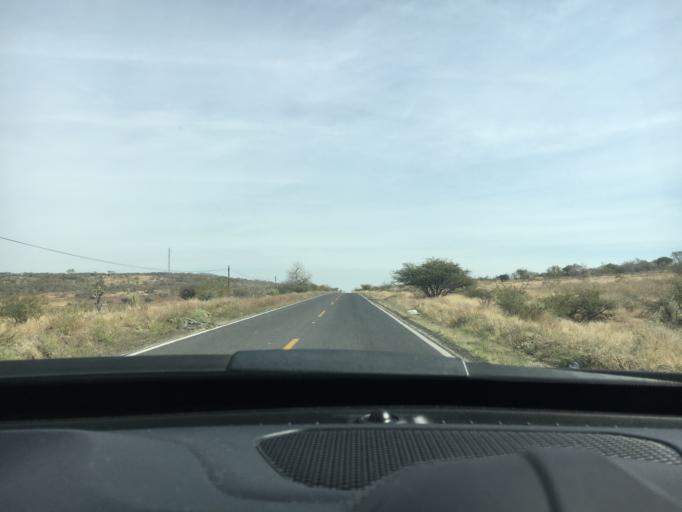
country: MX
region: Guanajuato
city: Duarte
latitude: 21.0575
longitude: -101.5086
